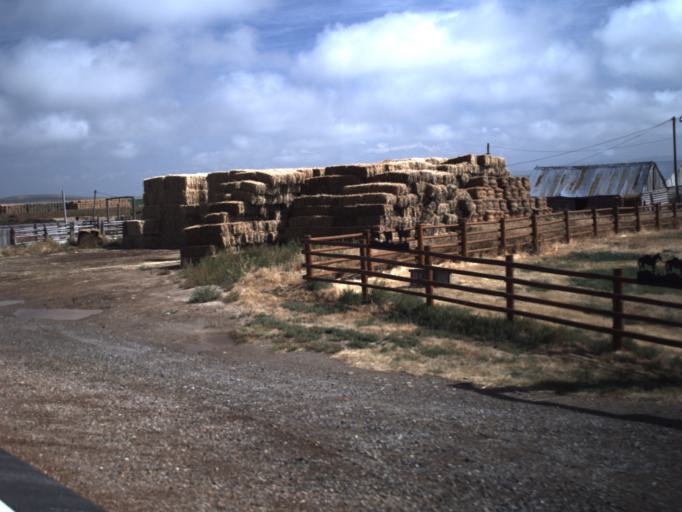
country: US
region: Utah
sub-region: Rich County
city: Randolph
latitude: 41.7325
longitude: -111.1593
